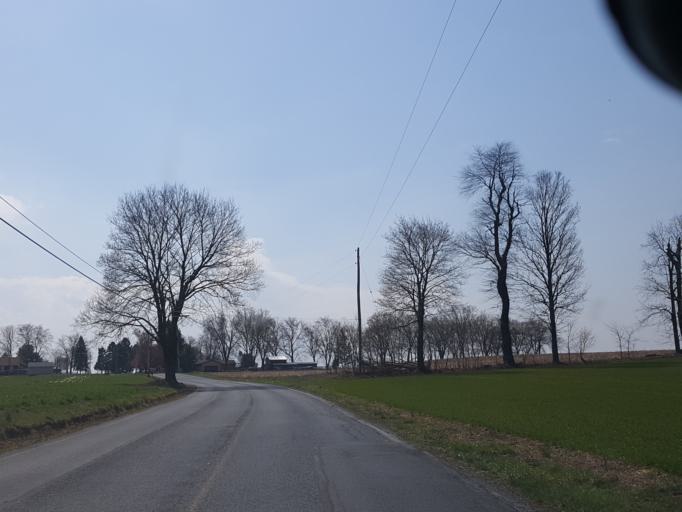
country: US
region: Pennsylvania
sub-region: Lebanon County
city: Annville
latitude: 40.3084
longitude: -76.5305
